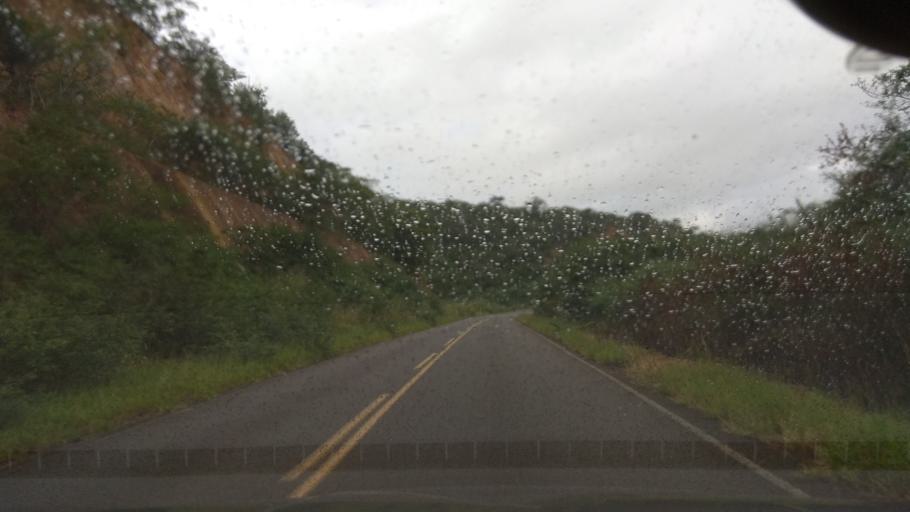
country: BR
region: Bahia
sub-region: Ubaira
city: Ubaira
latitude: -13.2423
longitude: -39.7386
